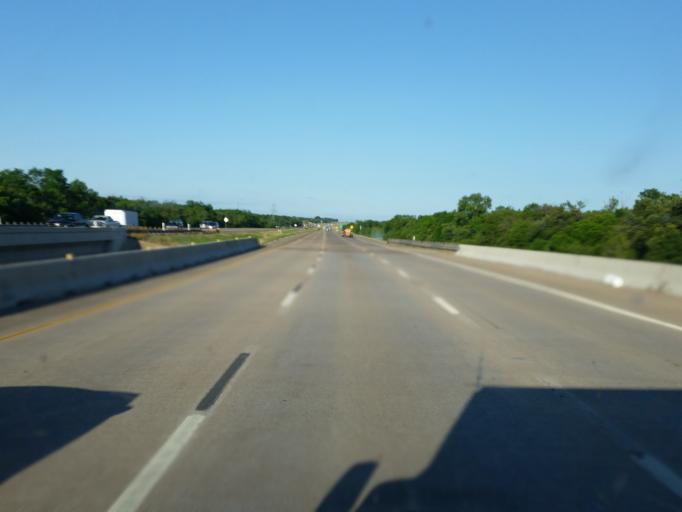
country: US
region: Texas
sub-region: Dallas County
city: Seagoville
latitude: 32.6998
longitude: -96.5309
